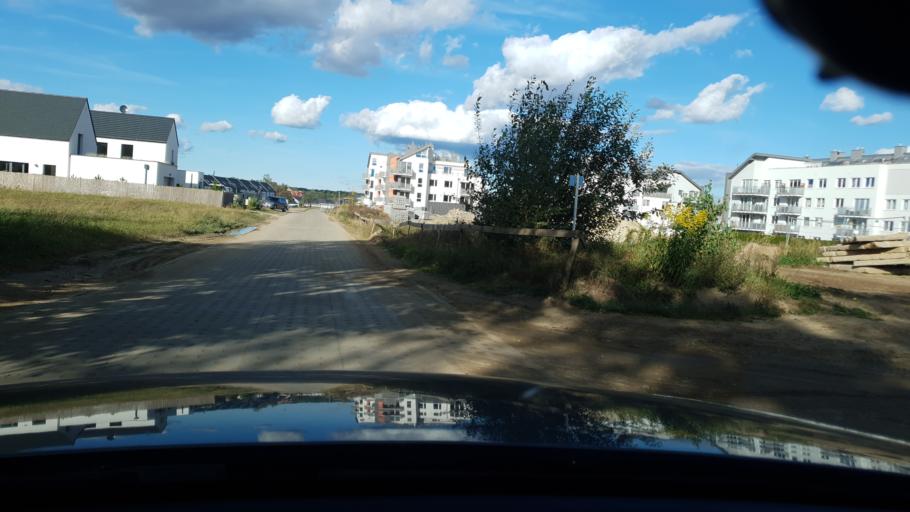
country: PL
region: Pomeranian Voivodeship
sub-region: Powiat wejherowski
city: Bojano
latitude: 54.4860
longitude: 18.4230
